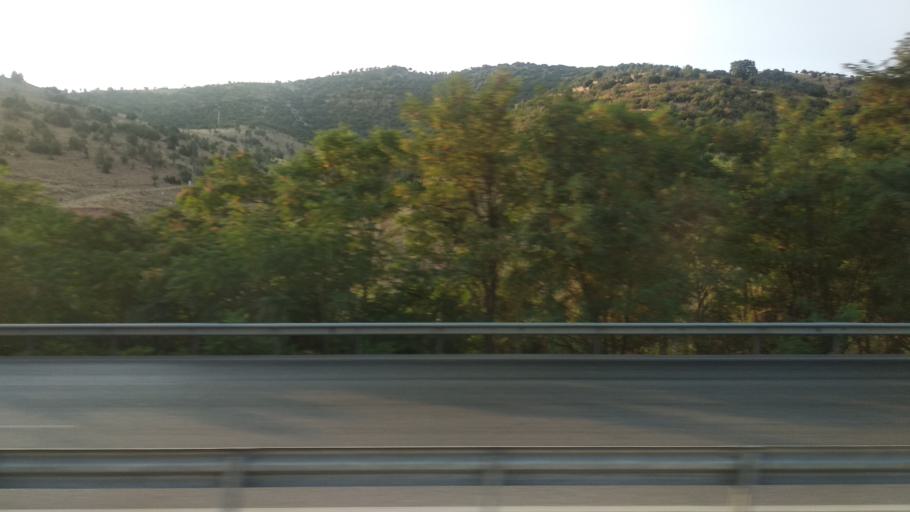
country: TR
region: Manisa
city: Menye
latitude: 38.5497
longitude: 28.4583
